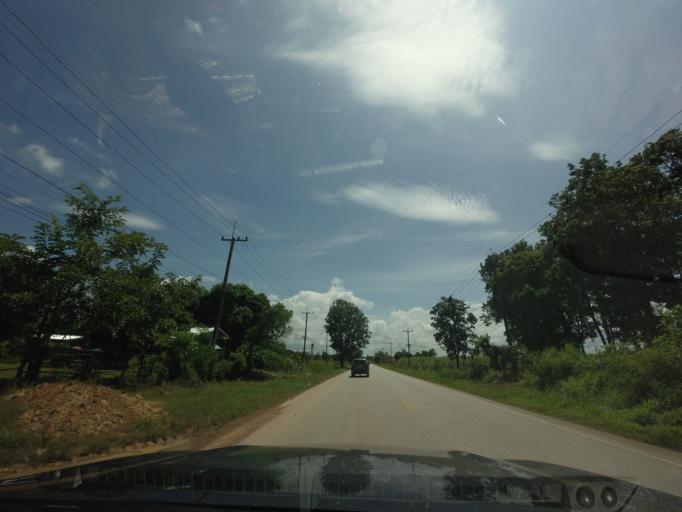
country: TH
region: Changwat Udon Thani
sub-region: Amphoe Ban Phue
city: Ban Phue
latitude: 17.7106
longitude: 102.4185
